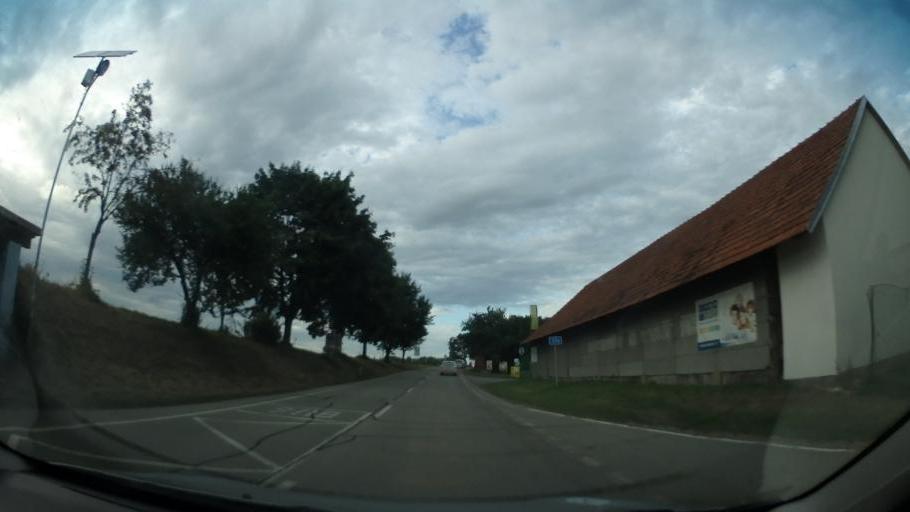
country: CZ
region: South Moravian
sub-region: Okres Blansko
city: Boskovice
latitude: 49.5303
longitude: 16.6860
